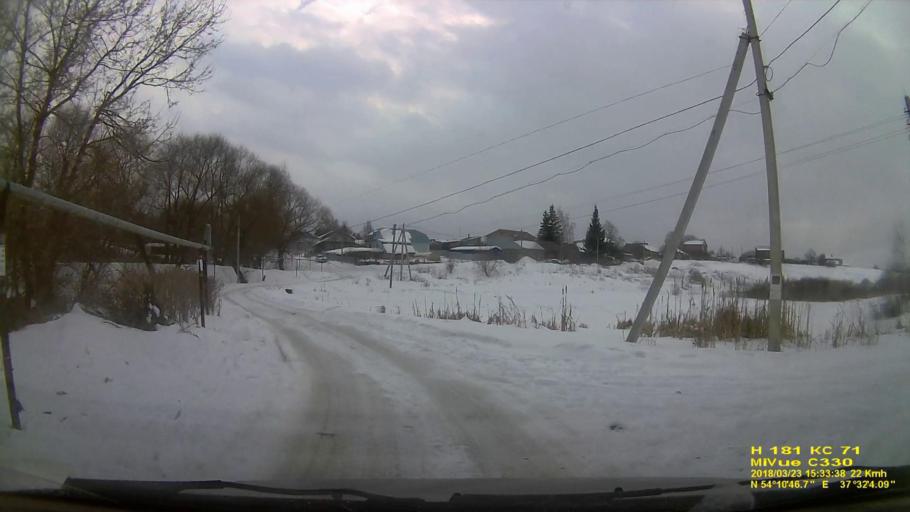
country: RU
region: Tula
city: Kosaya Gora
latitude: 54.1796
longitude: 37.5349
